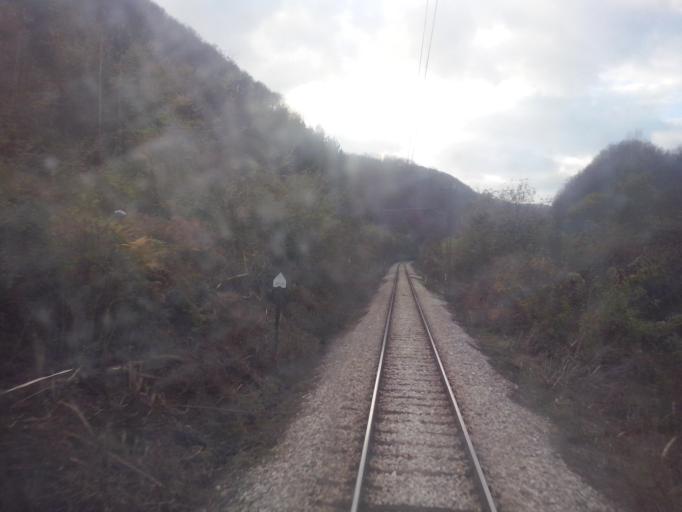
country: RS
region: Central Serbia
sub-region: Zlatiborski Okrug
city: Kosjeric
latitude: 43.9588
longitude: 19.9754
